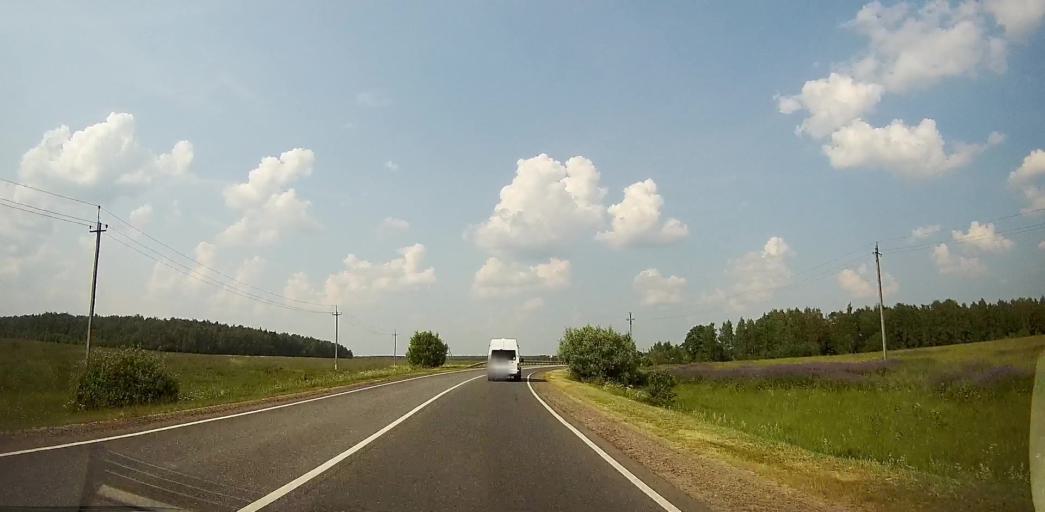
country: RU
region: Moskovskaya
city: Stupino
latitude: 54.9605
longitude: 38.1230
